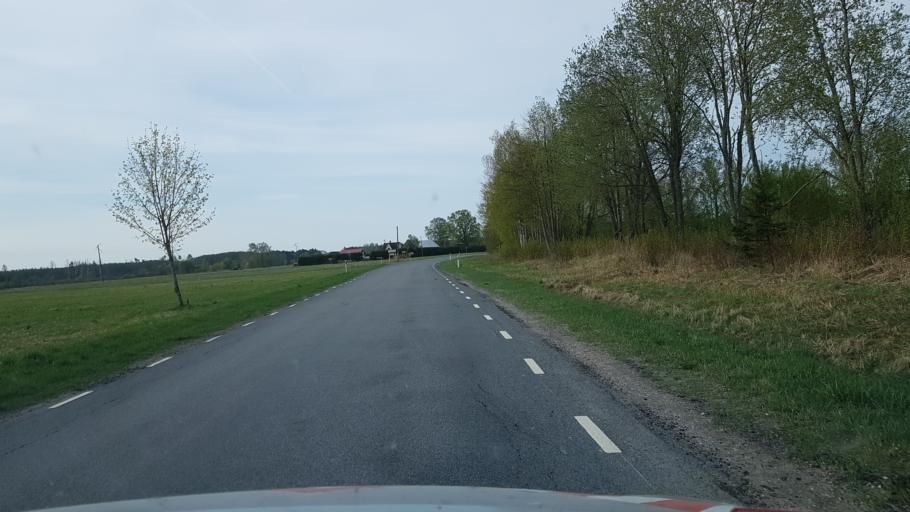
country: EE
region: Paernumaa
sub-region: Audru vald
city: Audru
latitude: 58.3648
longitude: 24.2635
